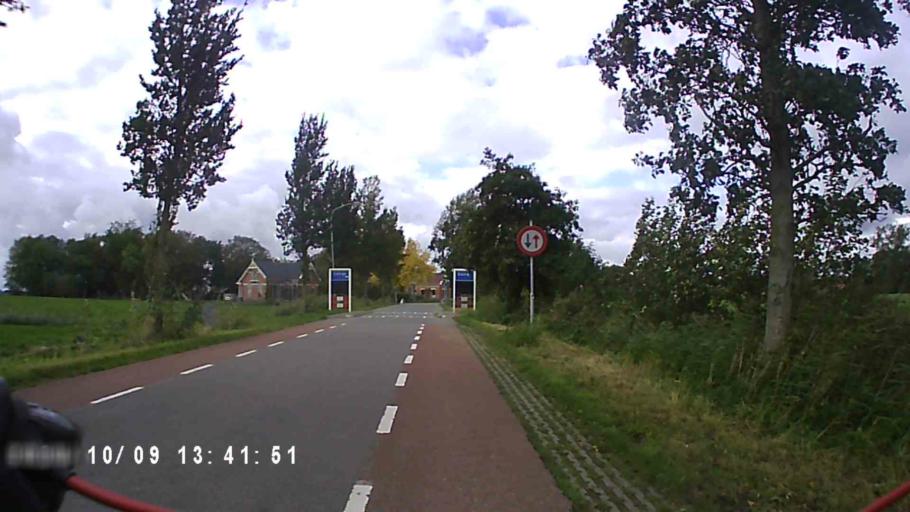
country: NL
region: Groningen
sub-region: Gemeente Zuidhorn
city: Aduard
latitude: 53.3043
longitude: 6.4499
